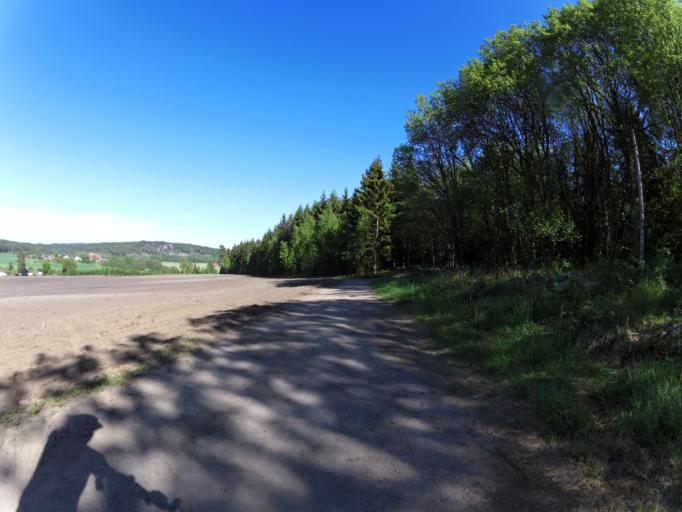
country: NO
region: Ostfold
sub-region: Sarpsborg
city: Sarpsborg
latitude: 59.2235
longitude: 11.0482
